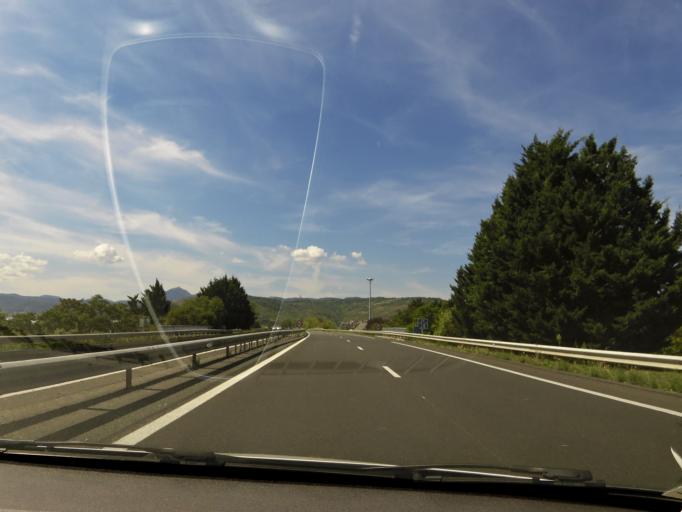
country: FR
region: Auvergne
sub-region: Departement du Puy-de-Dome
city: Gerzat
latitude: 45.8064
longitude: 3.1327
